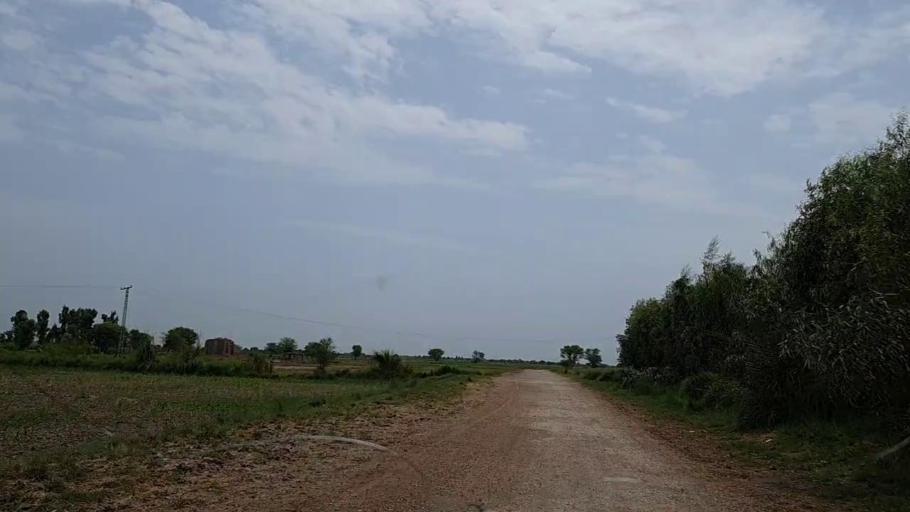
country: PK
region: Sindh
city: Tharu Shah
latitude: 26.9188
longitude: 68.0813
